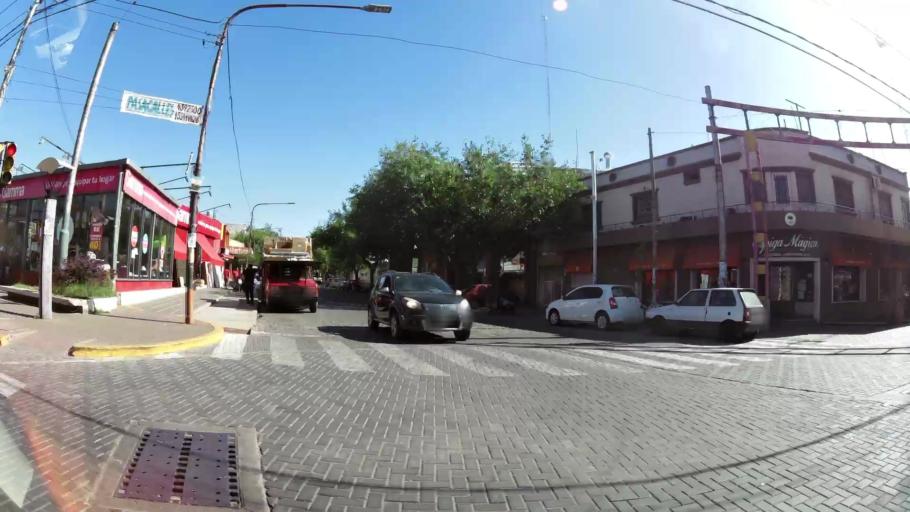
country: AR
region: Mendoza
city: Villa Nueva
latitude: -32.9032
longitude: -68.7891
